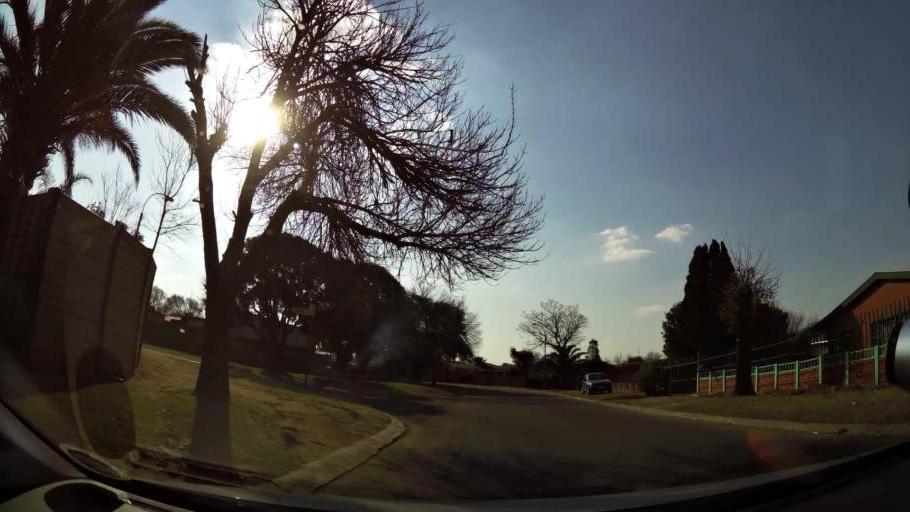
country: ZA
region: Gauteng
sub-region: City of Johannesburg Metropolitan Municipality
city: Modderfontein
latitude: -26.0872
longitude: 28.1934
